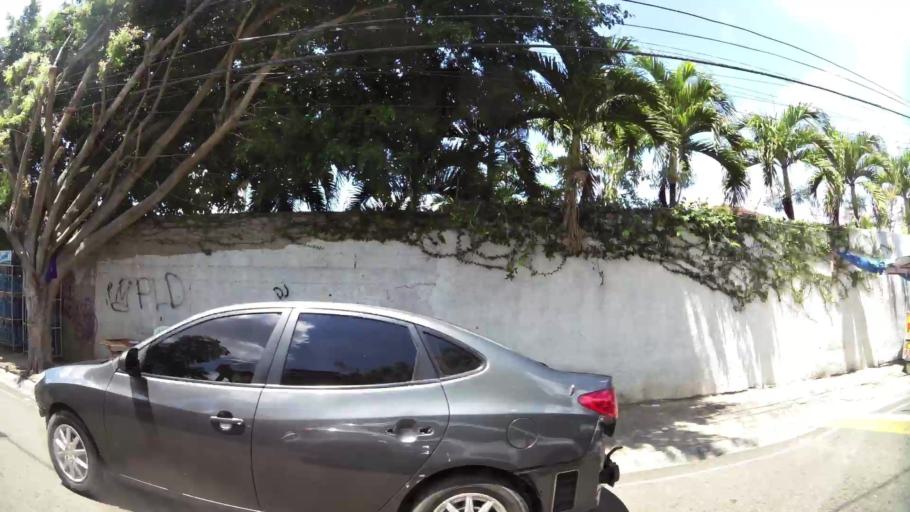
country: DO
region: Santiago
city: Santiago de los Caballeros
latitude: 19.4673
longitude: -70.6754
